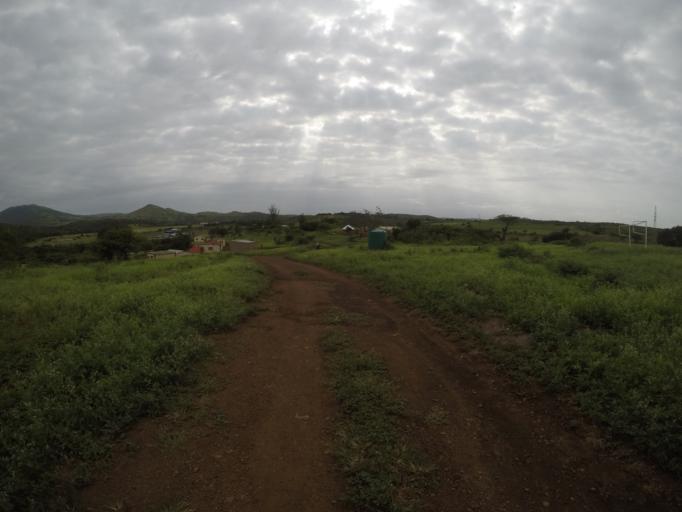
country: ZA
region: KwaZulu-Natal
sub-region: uThungulu District Municipality
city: Empangeni
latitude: -28.6403
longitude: 31.9081
